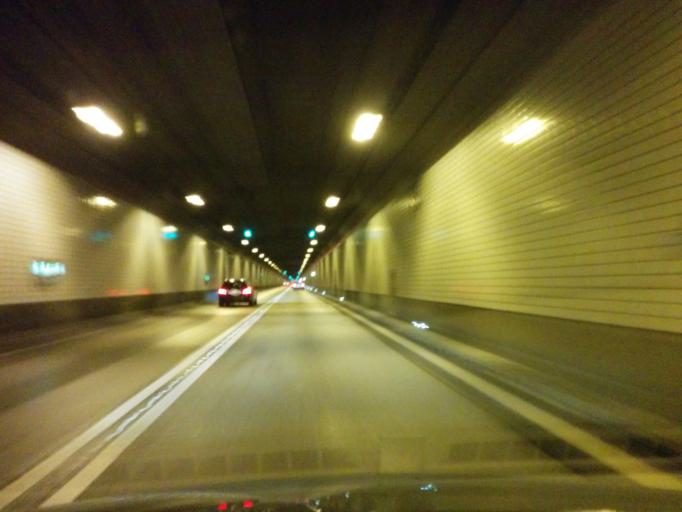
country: DE
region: Hamburg
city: Altona
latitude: 53.5535
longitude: 9.8974
